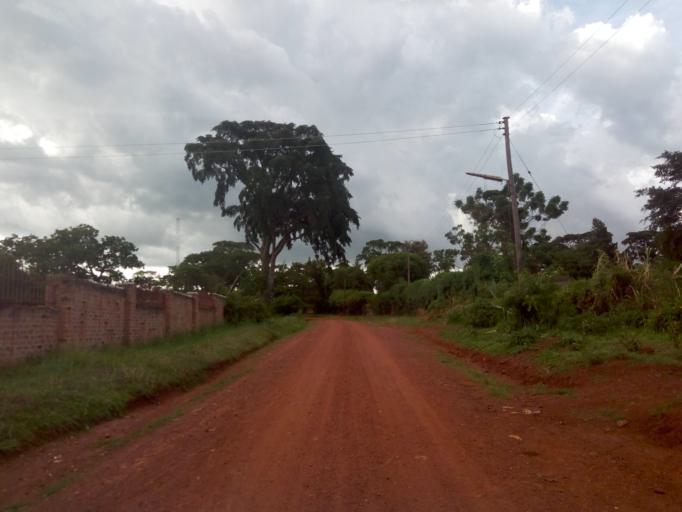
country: UG
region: Western Region
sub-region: Masindi District
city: Masindi
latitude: 1.6889
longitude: 31.7238
